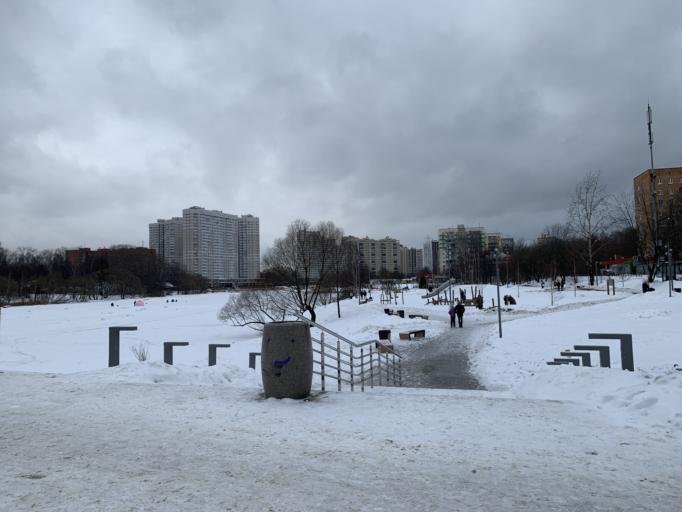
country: RU
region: Moskovskaya
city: Pushkino
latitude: 56.0070
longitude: 37.8643
